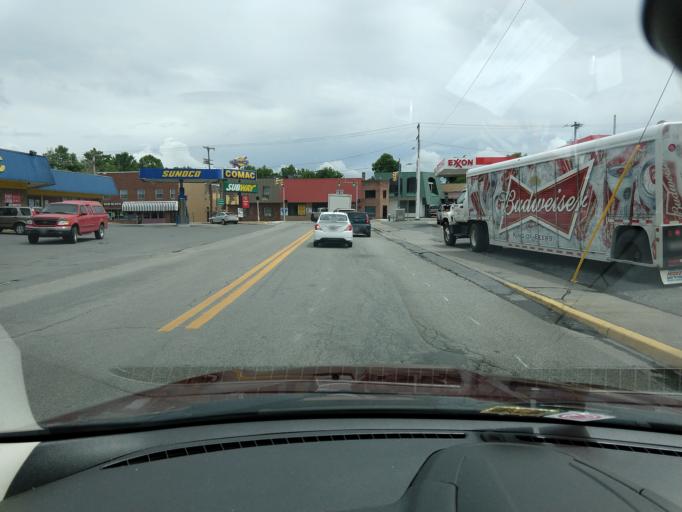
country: US
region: West Virginia
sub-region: Fayette County
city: Oak Hill
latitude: 37.9726
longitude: -81.1493
